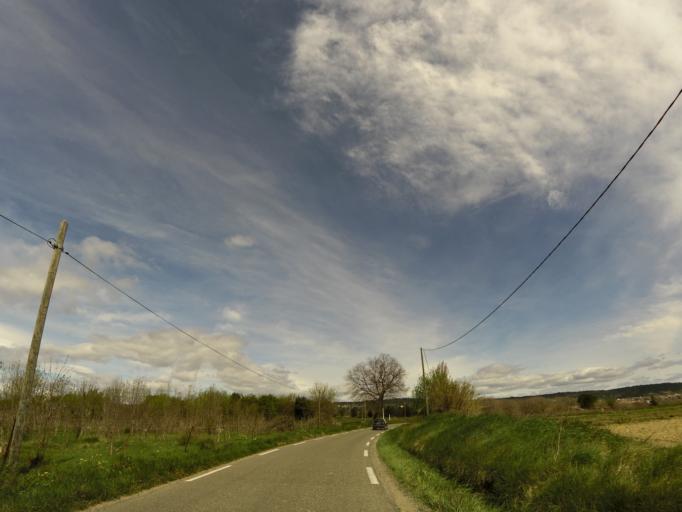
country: FR
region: Languedoc-Roussillon
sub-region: Departement du Gard
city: Calvisson
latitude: 43.8097
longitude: 4.1974
